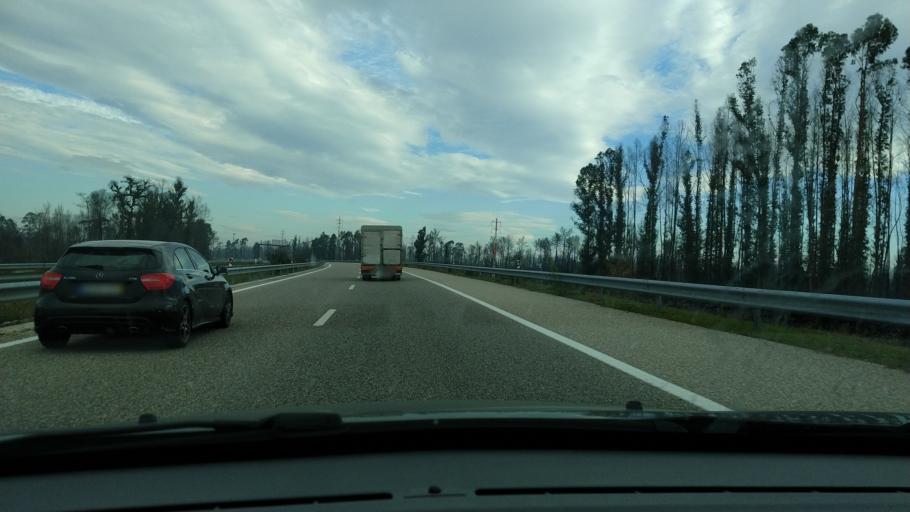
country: PT
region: Coimbra
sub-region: Mira
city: Mira
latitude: 40.4644
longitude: -8.6906
